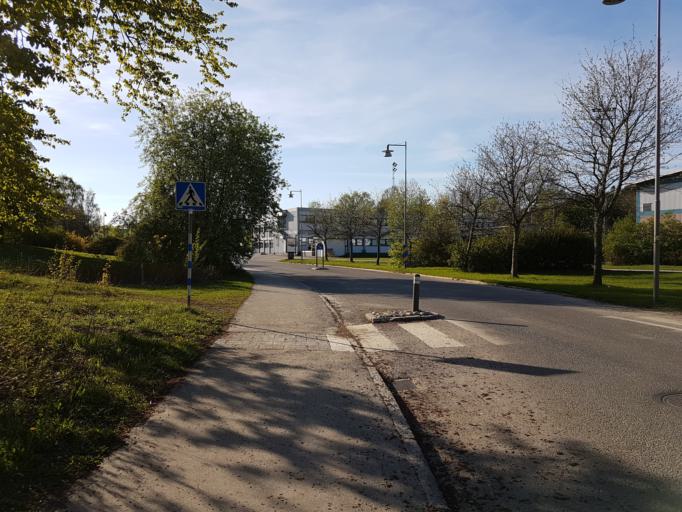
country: SE
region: Stockholm
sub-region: Solna Kommun
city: Rasunda
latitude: 59.3767
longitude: 17.9757
